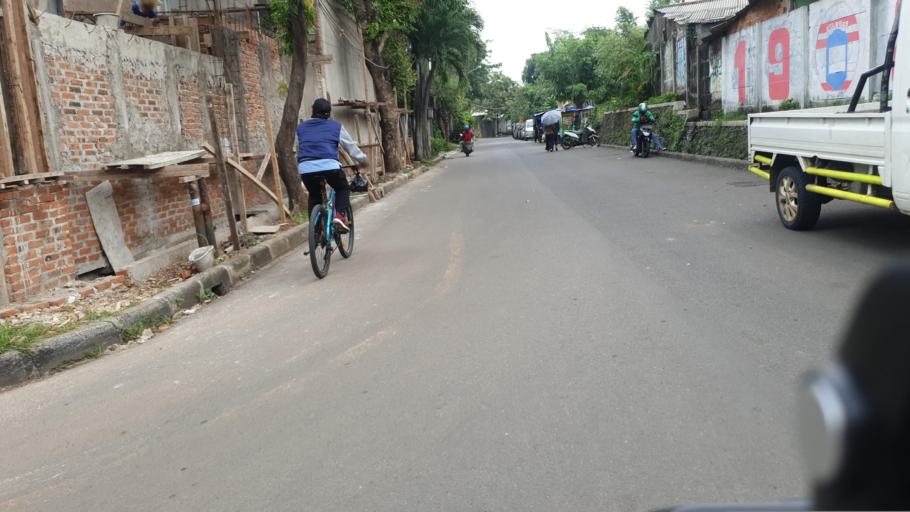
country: ID
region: West Java
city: Ciputat
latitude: -6.1946
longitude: 106.7511
